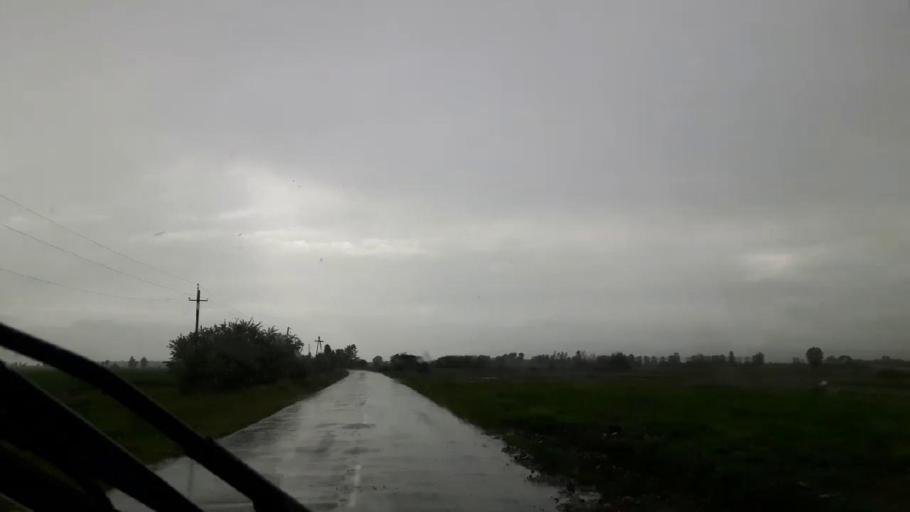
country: GE
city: Agara
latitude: 42.0145
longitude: 43.8090
